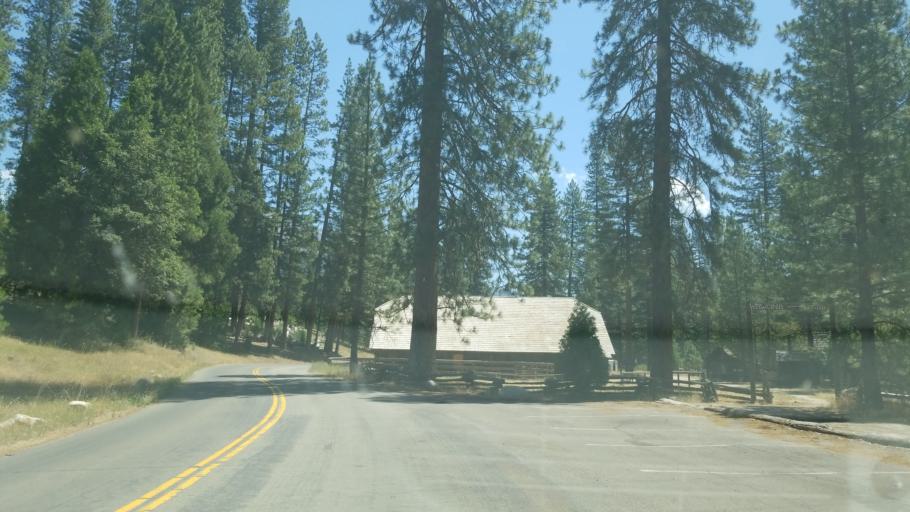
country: US
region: California
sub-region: Madera County
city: Ahwahnee
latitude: 37.5397
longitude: -119.6568
